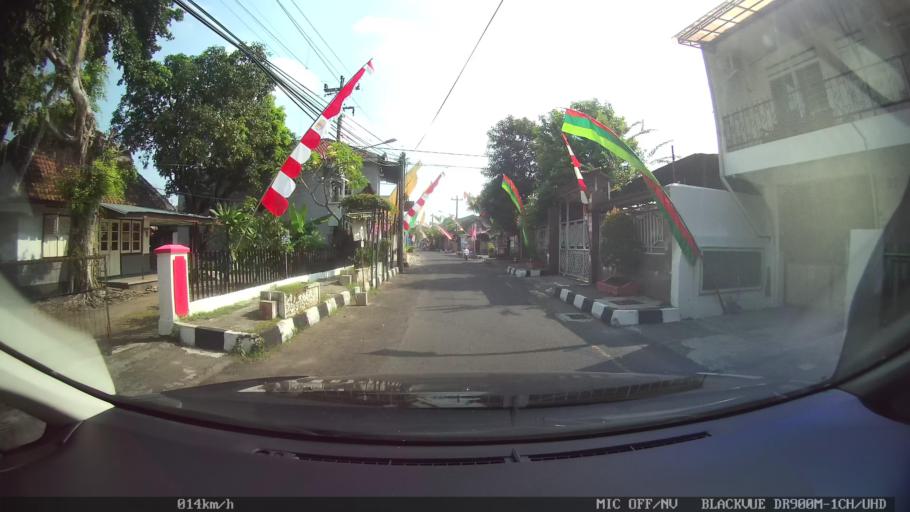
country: ID
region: Daerah Istimewa Yogyakarta
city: Yogyakarta
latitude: -7.8101
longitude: 110.3722
